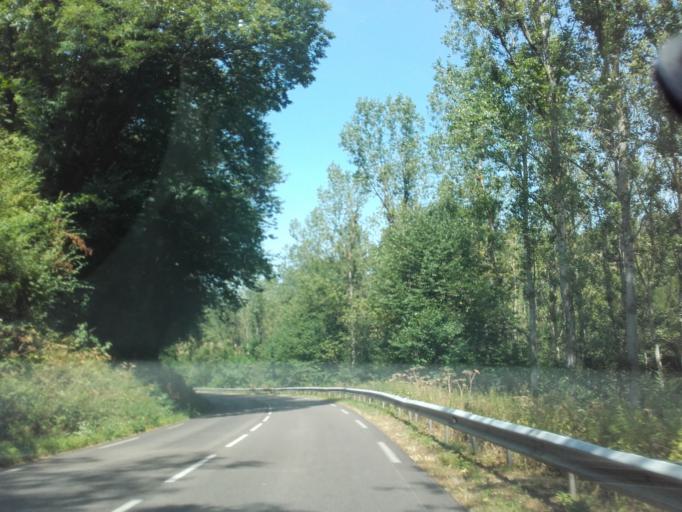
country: FR
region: Rhone-Alpes
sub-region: Departement de l'Isere
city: La Cote-Saint-Andre
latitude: 45.4102
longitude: 5.2670
